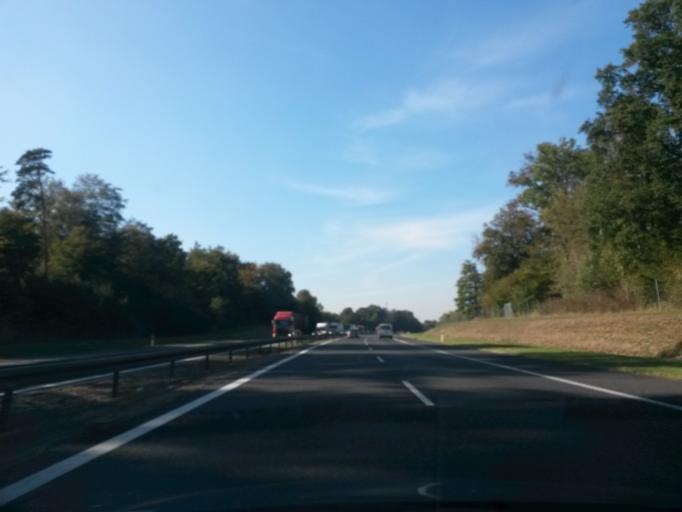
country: PL
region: Opole Voivodeship
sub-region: Powiat strzelecki
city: Ujazd
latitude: 50.4314
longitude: 18.3726
